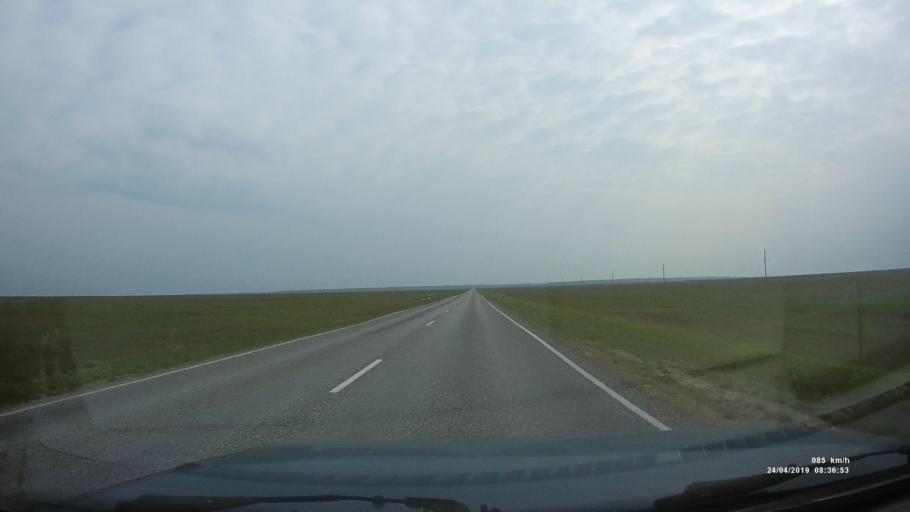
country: RU
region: Kalmykiya
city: Arshan'
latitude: 46.2070
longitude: 43.9418
